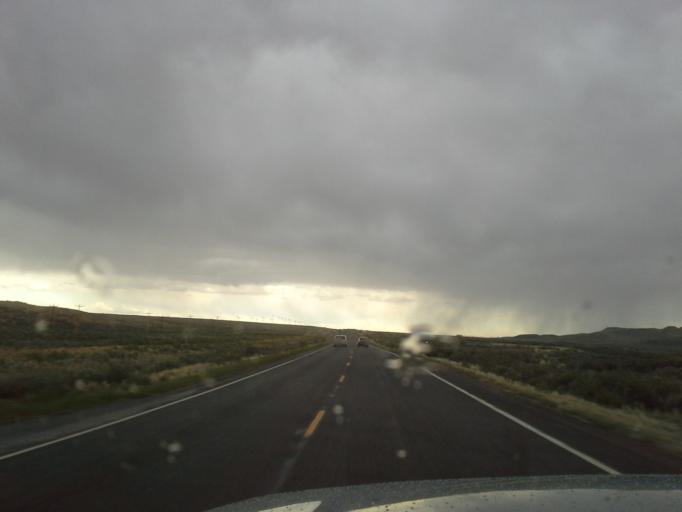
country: US
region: Wyoming
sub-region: Park County
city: Powell
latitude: 45.0458
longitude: -108.6515
